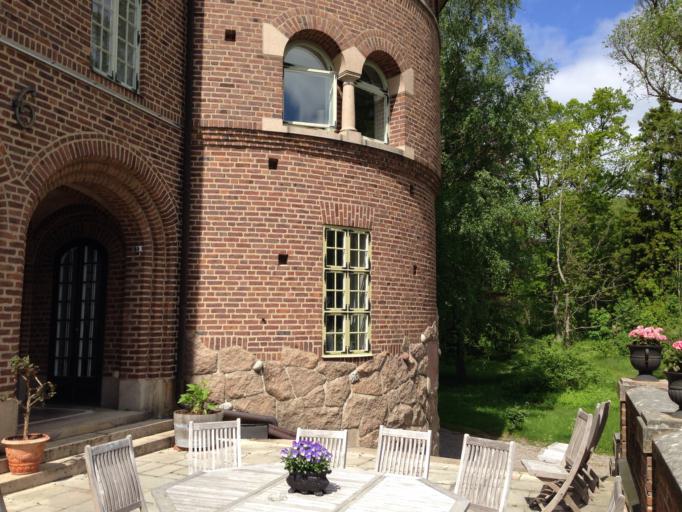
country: SE
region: Stockholm
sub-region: Sodertalje Kommun
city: Pershagen
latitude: 59.0681
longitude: 17.6665
